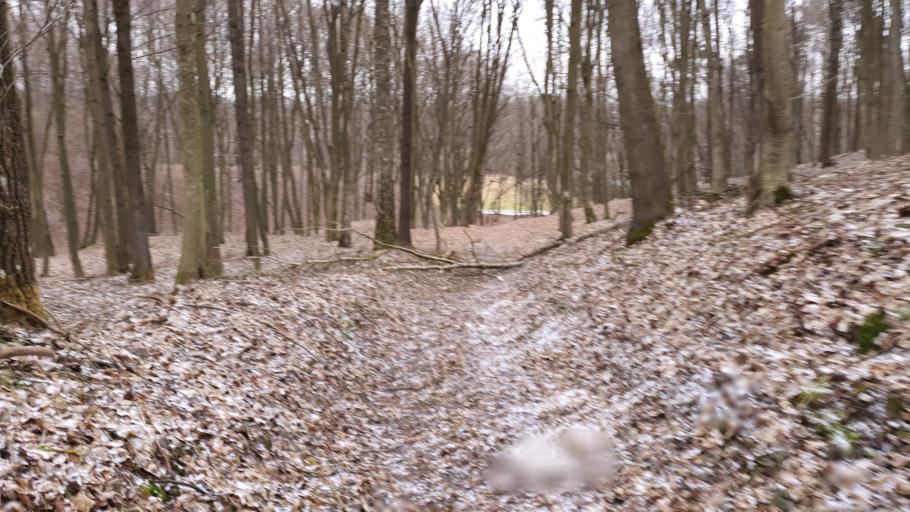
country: PL
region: Lublin Voivodeship
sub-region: Powiat pulawski
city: Naleczow
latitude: 51.2808
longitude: 22.2080
